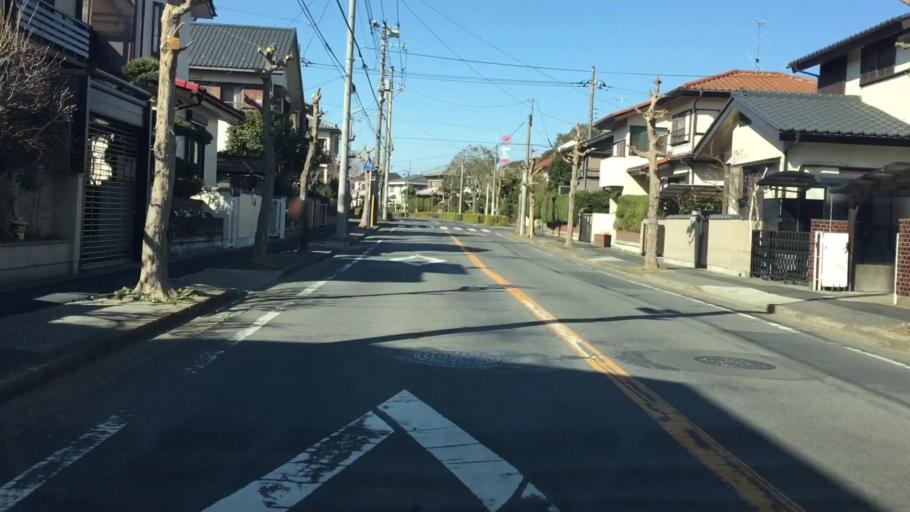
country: JP
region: Ibaraki
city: Fujishiro
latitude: 35.8549
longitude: 140.1285
